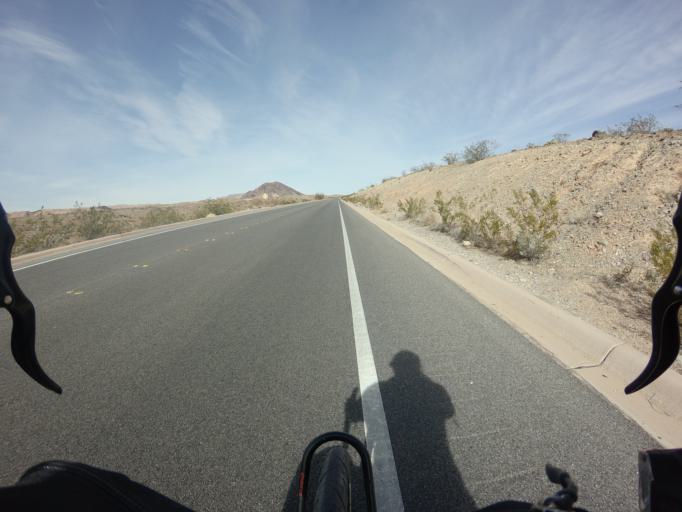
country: US
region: Nevada
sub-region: Clark County
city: Henderson
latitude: 36.1264
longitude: -114.9043
